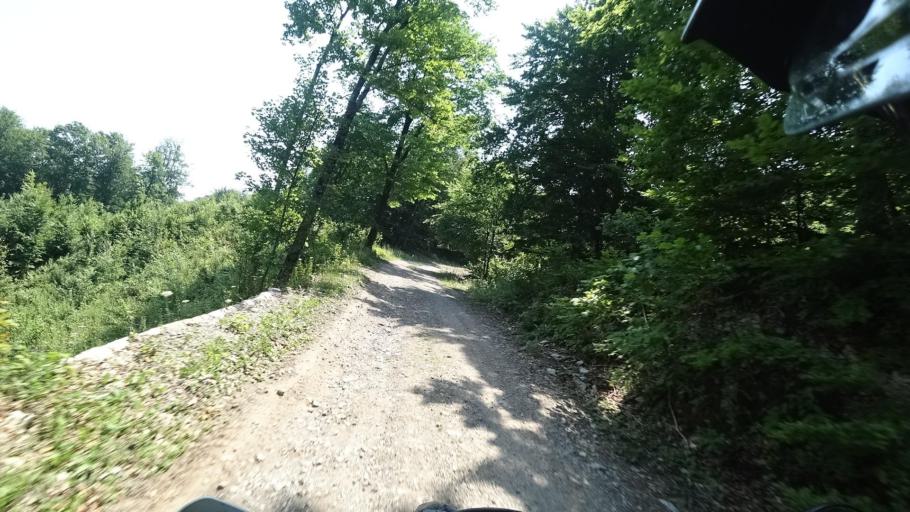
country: HR
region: Primorsko-Goranska
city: Vrbovsko
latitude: 45.3011
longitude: 15.1313
